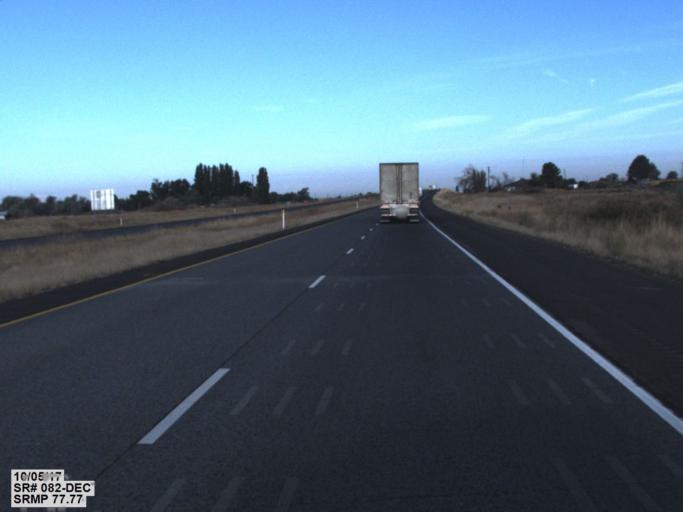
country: US
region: Washington
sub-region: Benton County
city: Prosser
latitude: 46.2403
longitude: -119.8265
